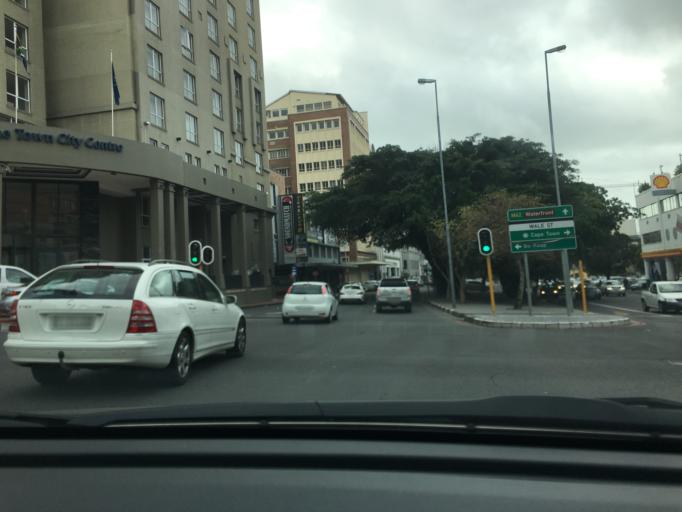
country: ZA
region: Western Cape
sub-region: City of Cape Town
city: Cape Town
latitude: -33.9219
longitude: 18.4158
